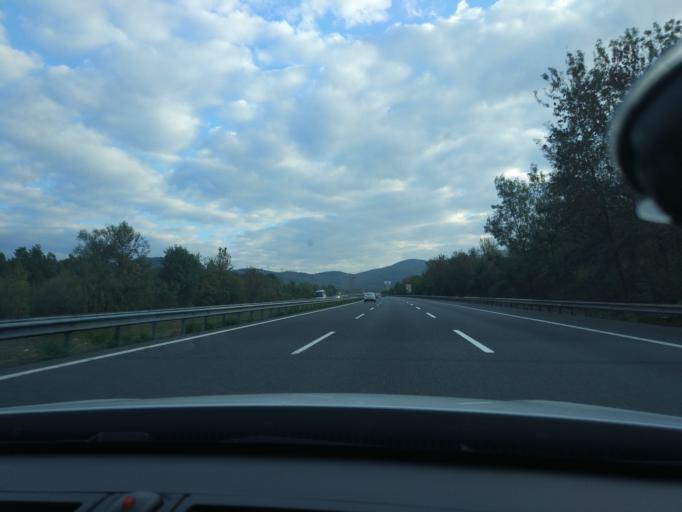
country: TR
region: Sakarya
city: Karadere
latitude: 40.7963
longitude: 30.8440
